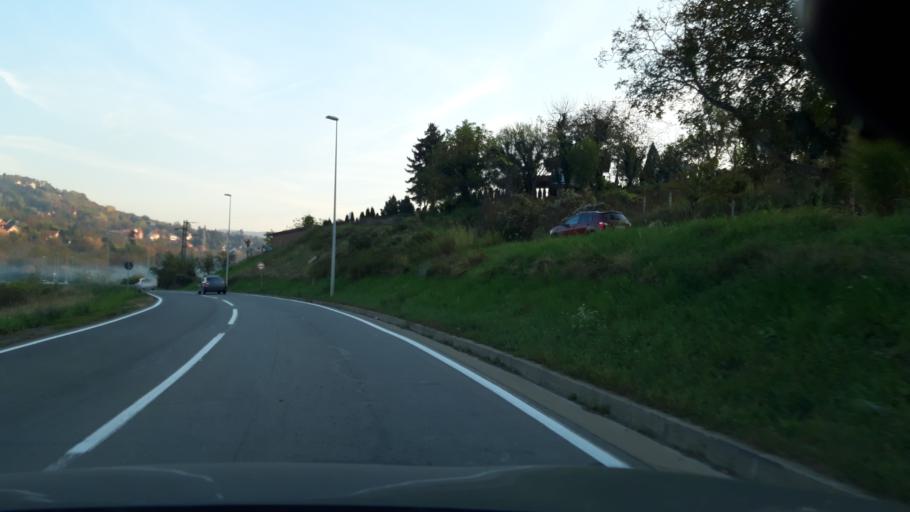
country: RS
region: Autonomna Pokrajina Vojvodina
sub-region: Juznobacki Okrug
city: Novi Sad
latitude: 45.2126
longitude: 19.8386
